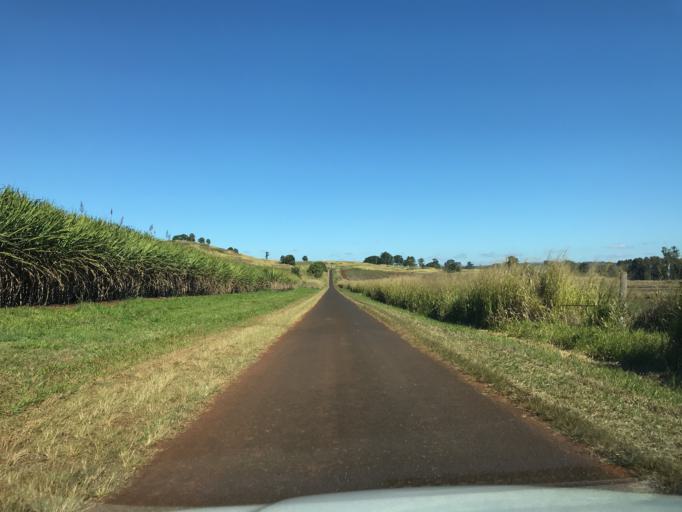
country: AU
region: Queensland
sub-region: Tablelands
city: Atherton
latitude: -17.2859
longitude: 145.5424
